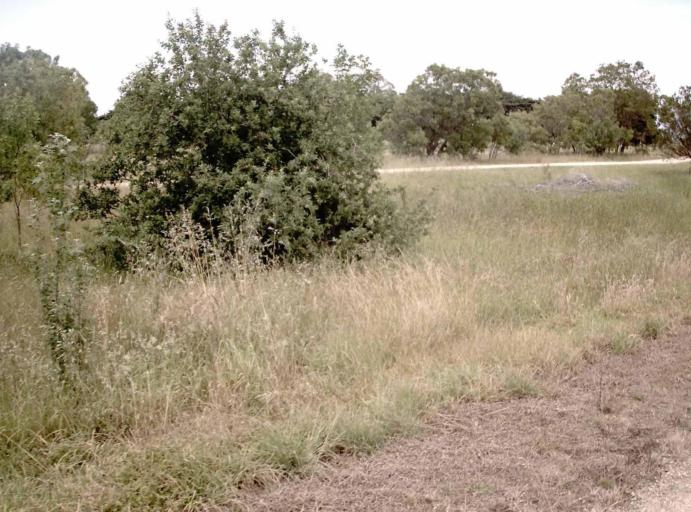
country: AU
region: Victoria
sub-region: Wellington
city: Sale
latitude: -37.9746
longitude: 147.0095
